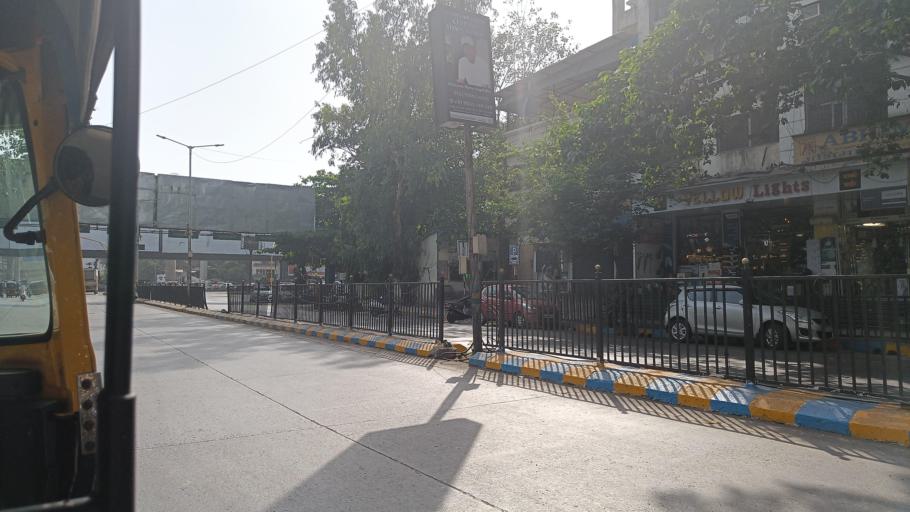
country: IN
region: Maharashtra
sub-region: Thane
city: Thane
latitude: 19.1889
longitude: 72.9647
